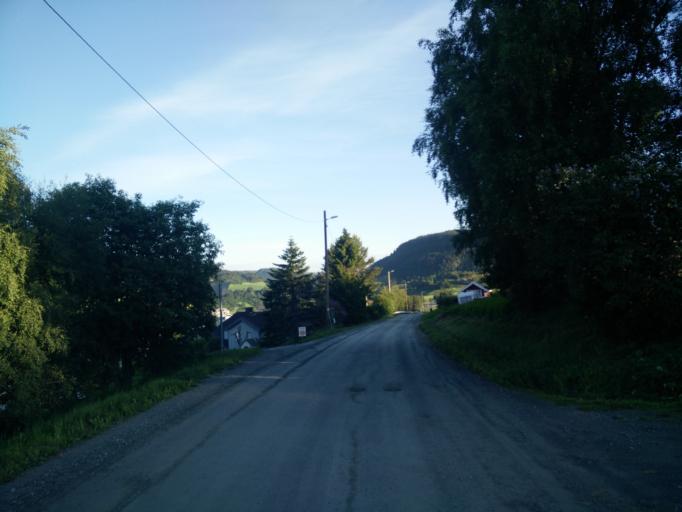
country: NO
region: Sor-Trondelag
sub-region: Skaun
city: Borsa
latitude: 63.3297
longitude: 10.0645
